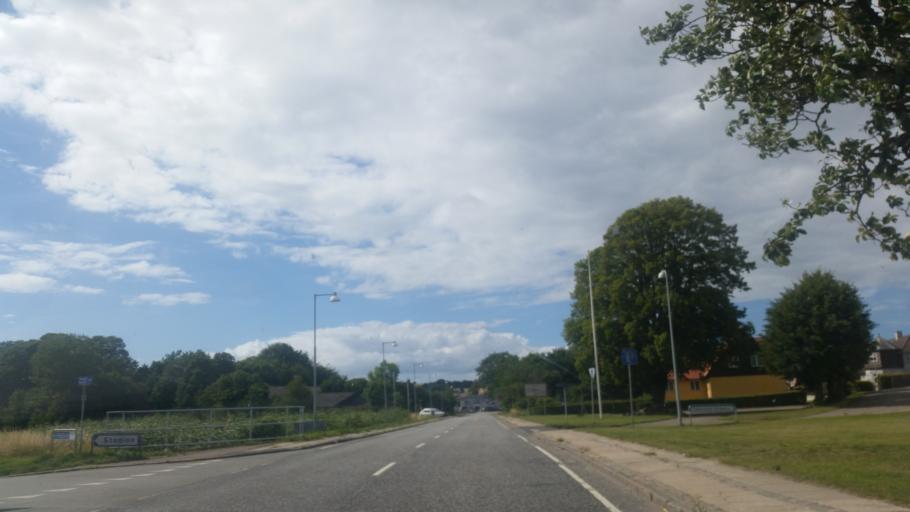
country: DK
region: Zealand
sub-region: Odsherred Kommune
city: Horve
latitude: 55.8020
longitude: 11.4423
